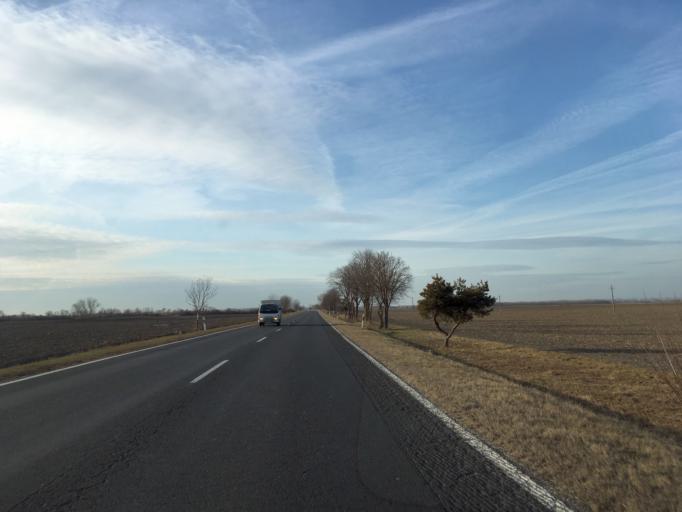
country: HU
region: Gyor-Moson-Sopron
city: Kimle
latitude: 47.7937
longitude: 17.3965
